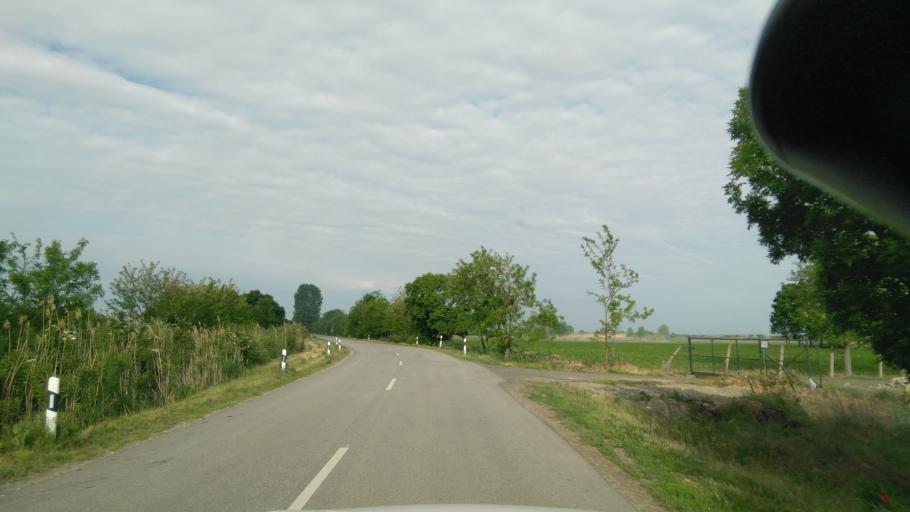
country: HU
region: Bekes
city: Ketegyhaza
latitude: 46.5393
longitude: 21.1482
